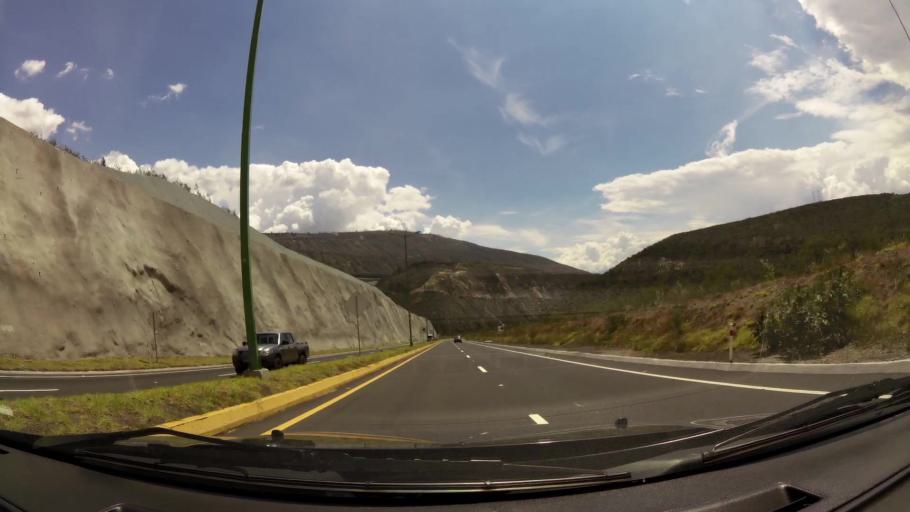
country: EC
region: Pichincha
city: Quito
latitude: -0.1025
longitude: -78.3817
